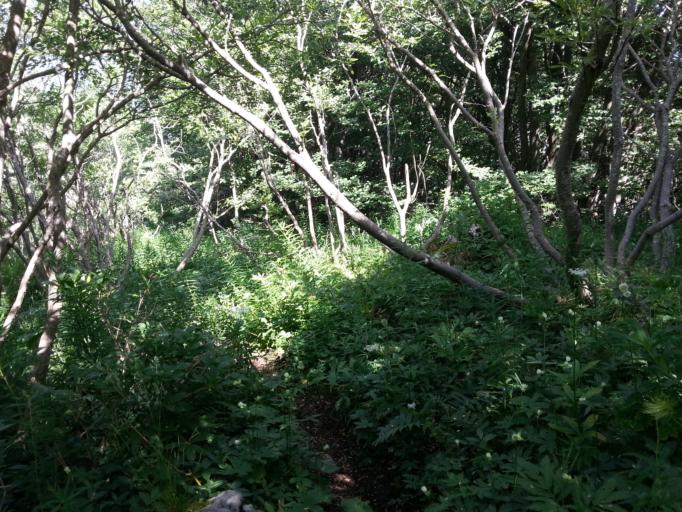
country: IT
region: Lombardy
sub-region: Provincia di Lecco
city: Ballabio
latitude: 45.9034
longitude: 9.4491
